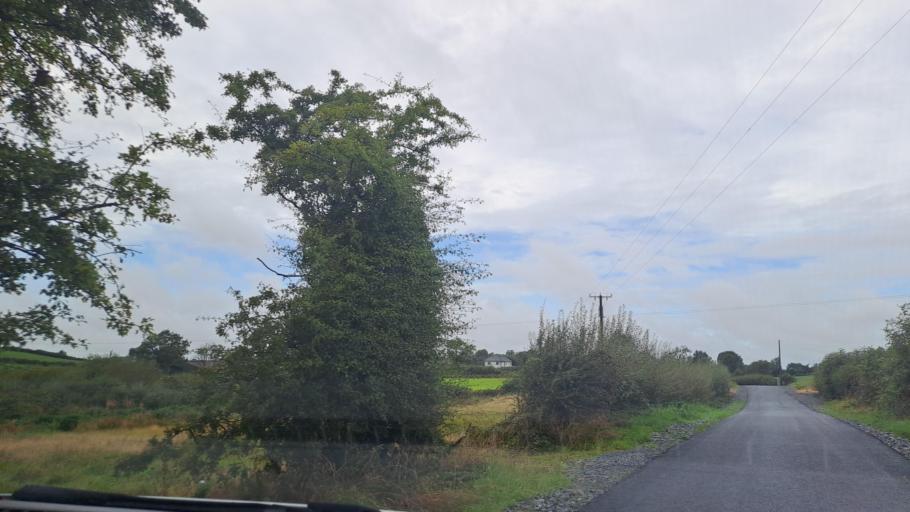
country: IE
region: Ulster
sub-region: An Cabhan
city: Kingscourt
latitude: 53.9807
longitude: -6.8290
